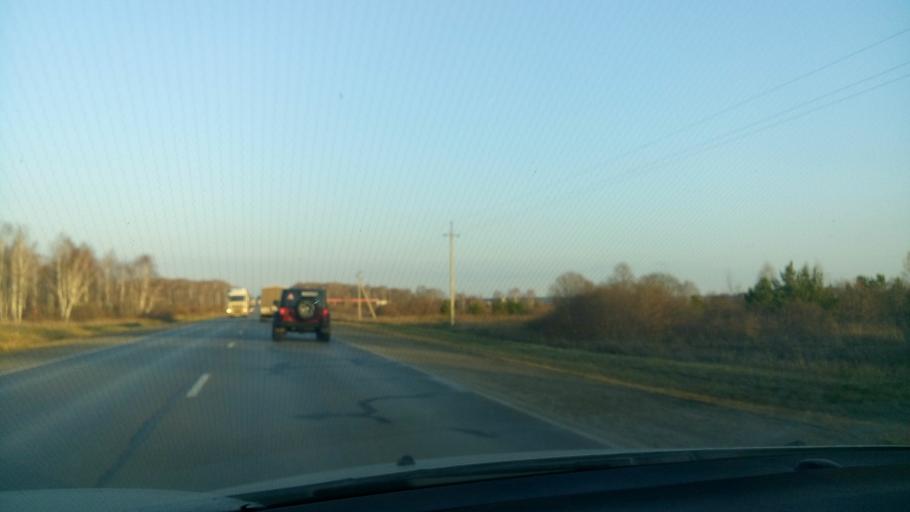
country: RU
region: Sverdlovsk
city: Bogdanovich
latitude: 56.7554
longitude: 62.1897
